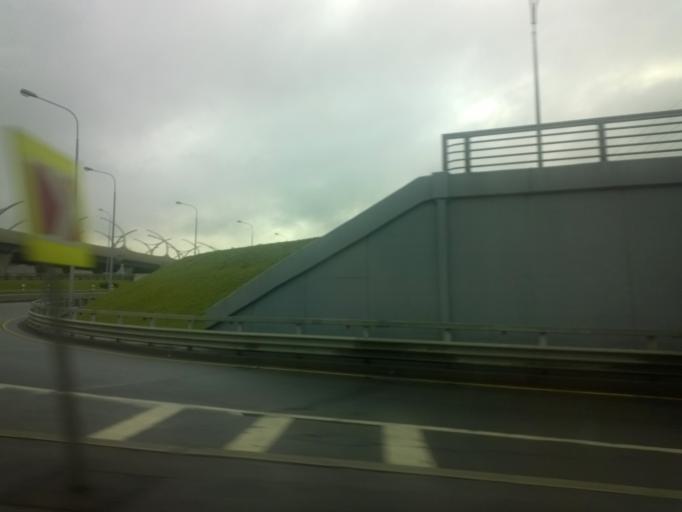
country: RU
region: St.-Petersburg
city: Avtovo
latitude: 59.8555
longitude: 30.2900
